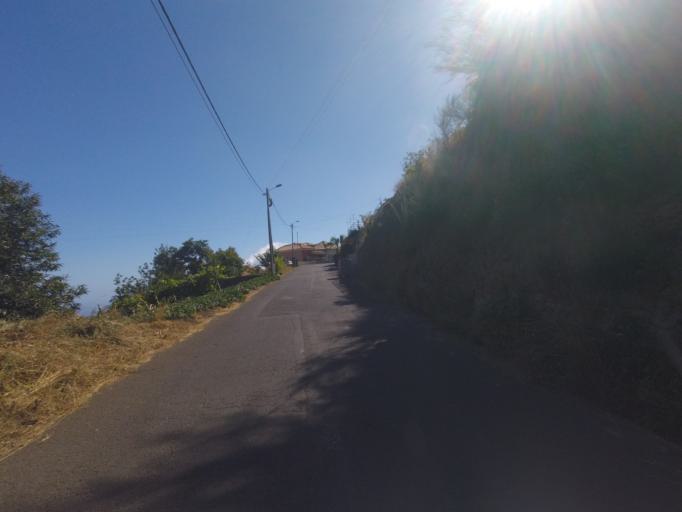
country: PT
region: Madeira
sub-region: Ribeira Brava
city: Campanario
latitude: 32.6964
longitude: -17.0188
